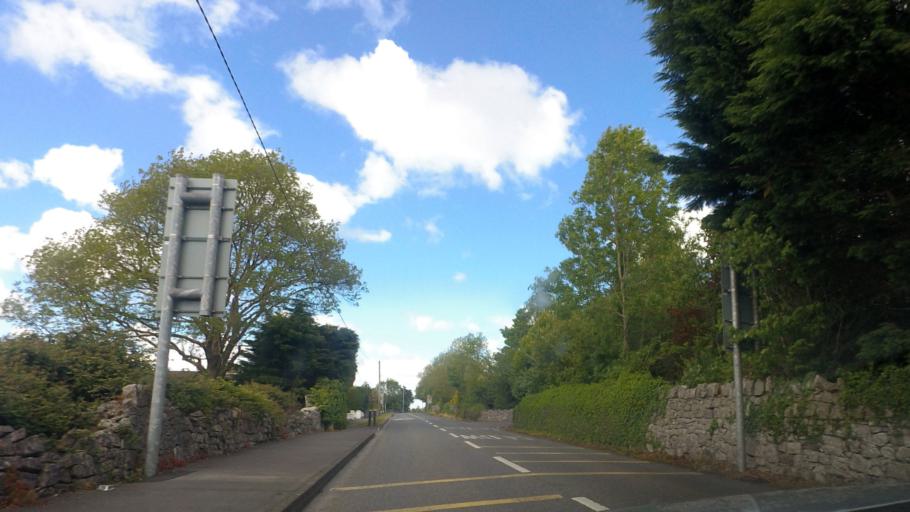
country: IE
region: Munster
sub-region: An Clar
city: Ennis
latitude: 52.8367
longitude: -9.0055
